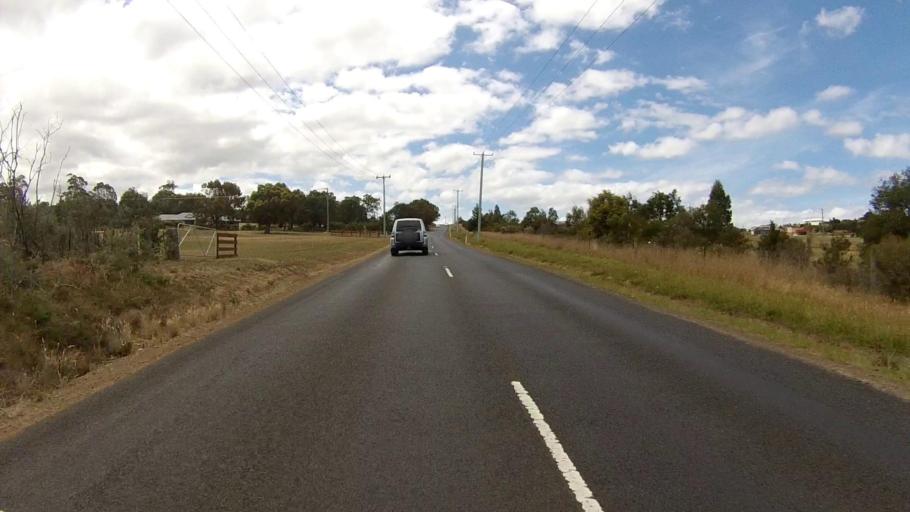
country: AU
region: Tasmania
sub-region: Sorell
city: Sorell
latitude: -42.8178
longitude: 147.6122
